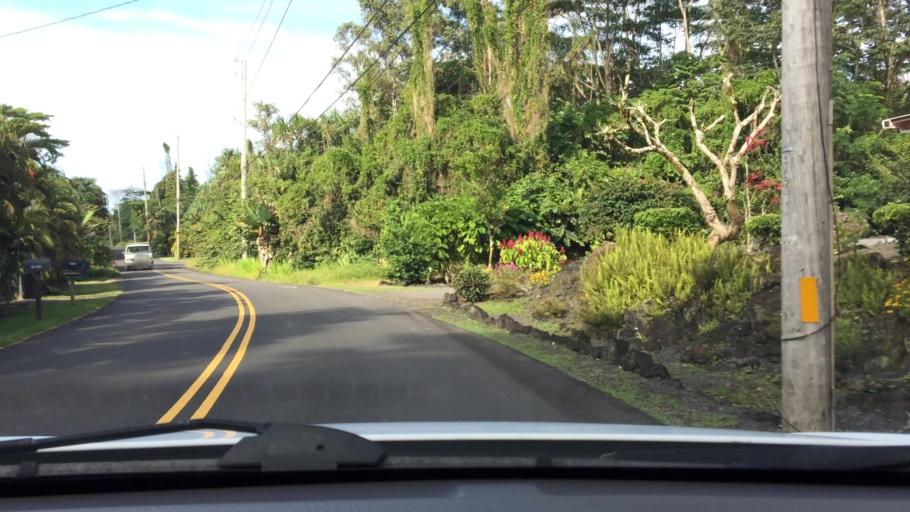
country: US
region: Hawaii
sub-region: Hawaii County
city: Hawaiian Beaches
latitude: 19.5459
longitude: -154.9016
